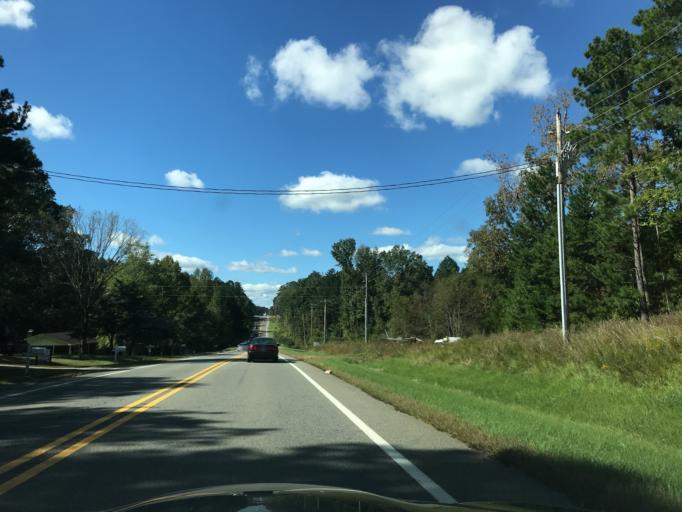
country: US
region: North Carolina
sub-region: Durham County
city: Gorman
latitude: 35.9782
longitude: -78.7692
